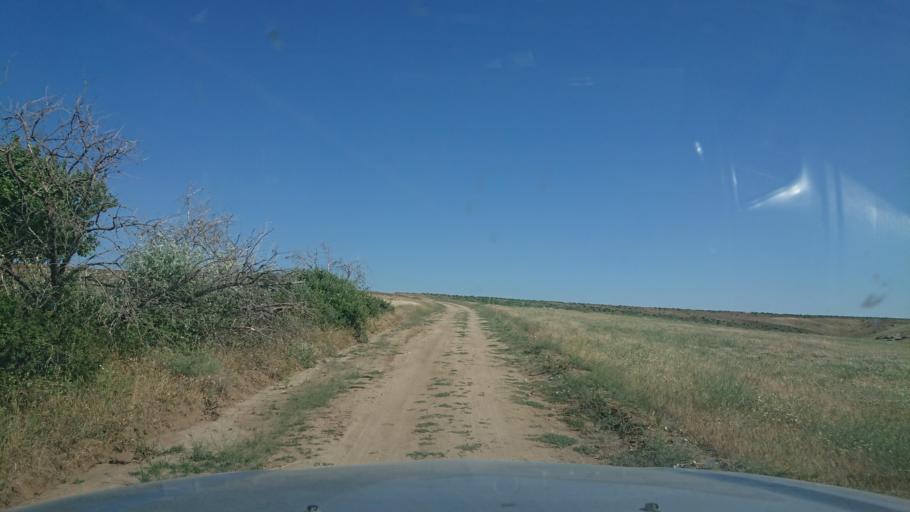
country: TR
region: Aksaray
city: Agacoren
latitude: 38.8465
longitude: 33.9181
